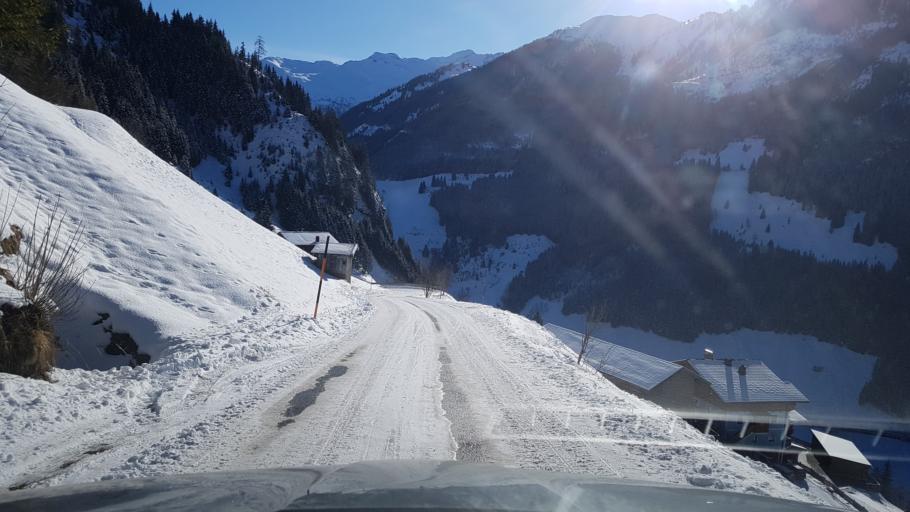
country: AT
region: Salzburg
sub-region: Politischer Bezirk Sankt Johann im Pongau
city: Huttschlag
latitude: 47.1732
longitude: 13.2656
